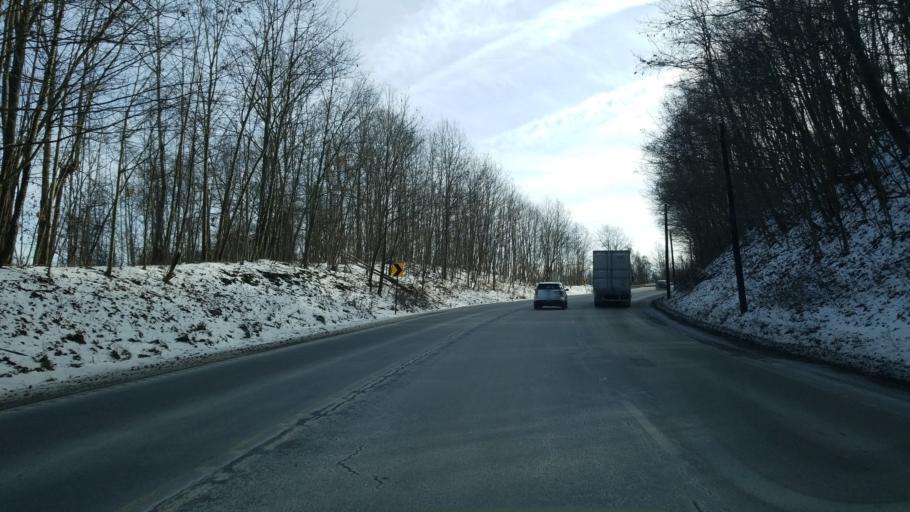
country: US
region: Pennsylvania
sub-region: Clearfield County
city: Treasure Lake
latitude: 41.1980
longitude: -78.5543
